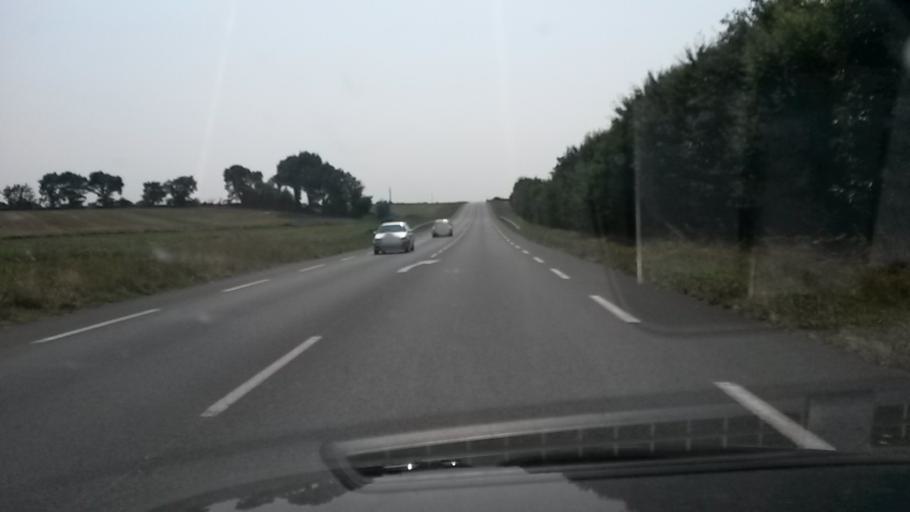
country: FR
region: Pays de la Loire
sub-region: Departement de la Mayenne
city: Chemaze
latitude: 47.7674
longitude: -0.7838
